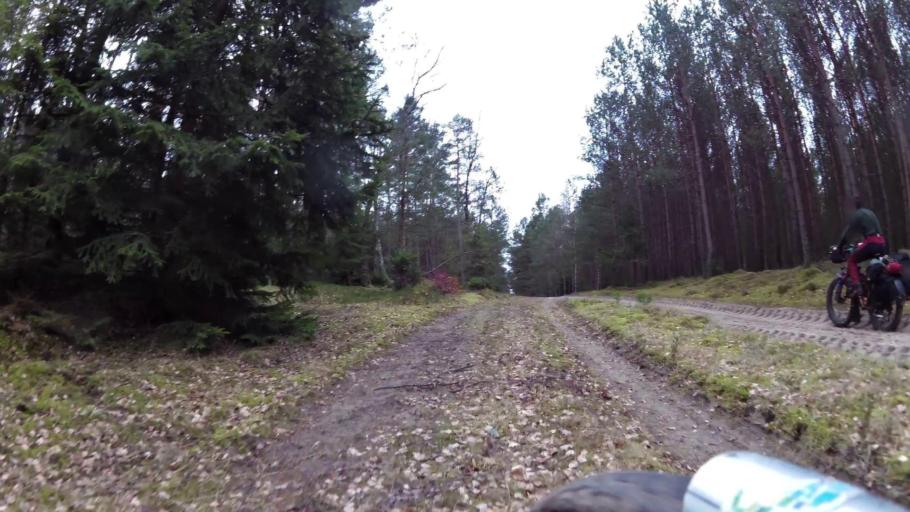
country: PL
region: Pomeranian Voivodeship
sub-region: Powiat bytowski
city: Trzebielino
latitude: 54.1275
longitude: 17.1345
